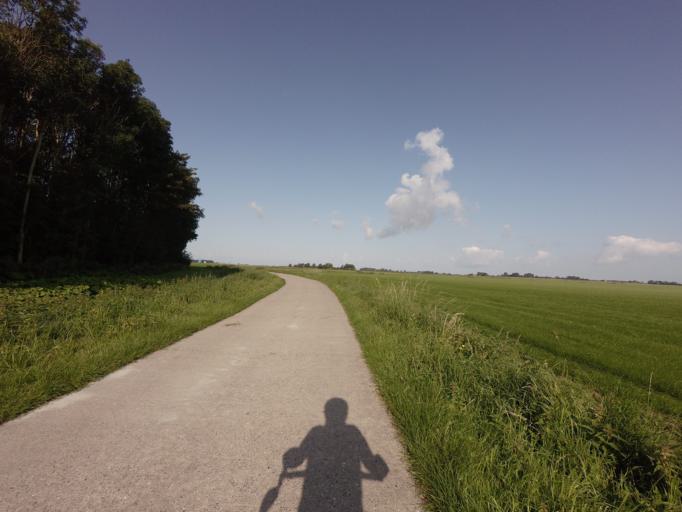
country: NL
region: Friesland
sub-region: Gemeente Franekeradeel
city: Franeker
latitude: 53.2018
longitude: 5.5787
